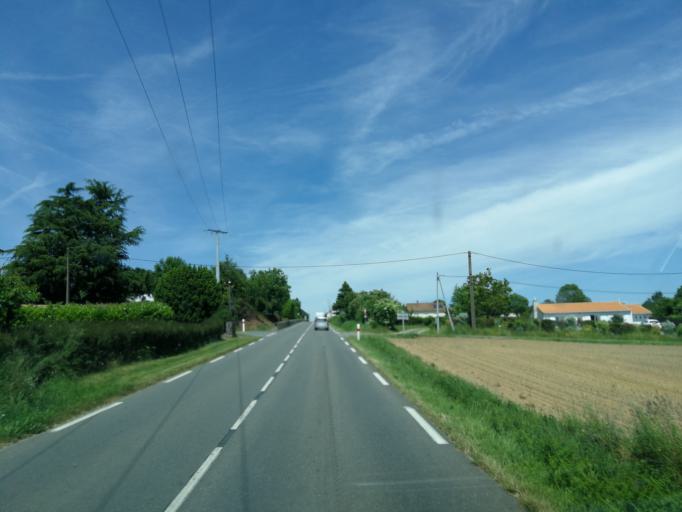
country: FR
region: Pays de la Loire
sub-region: Departement de la Vendee
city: Saint-Pierre-du-Chemin
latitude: 46.6876
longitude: -0.7084
